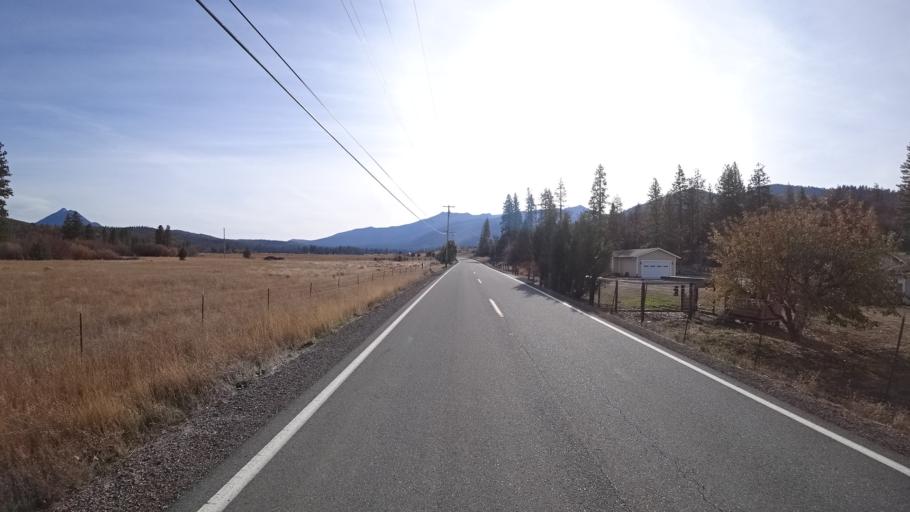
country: US
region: California
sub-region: Siskiyou County
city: Weed
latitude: 41.4321
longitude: -122.4368
